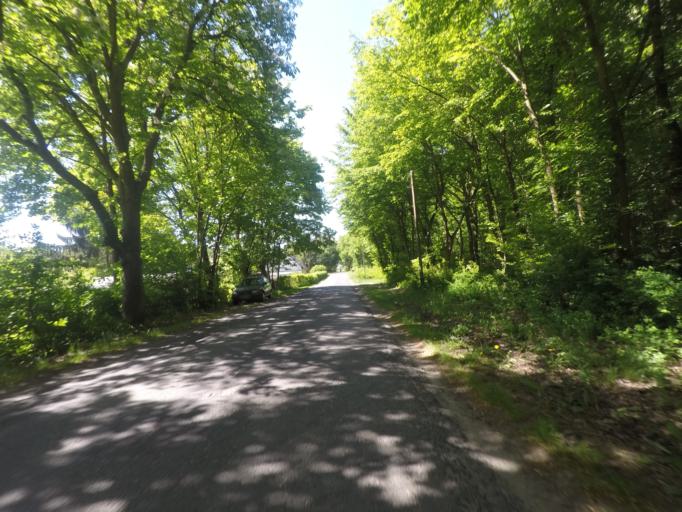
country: DE
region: Brandenburg
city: Melchow
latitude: 52.8495
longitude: 13.7141
